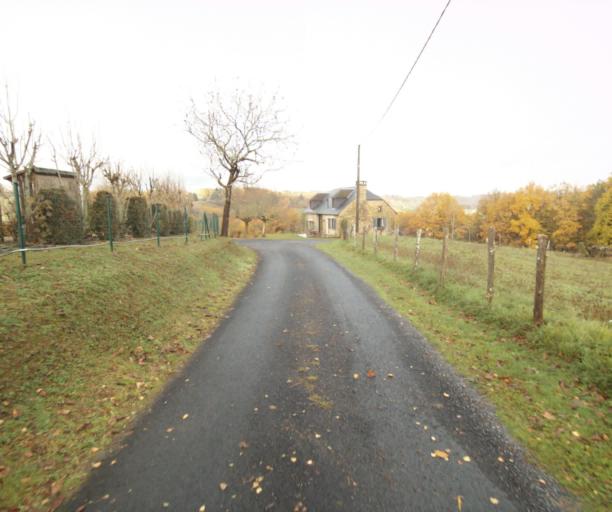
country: FR
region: Limousin
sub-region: Departement de la Correze
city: Cornil
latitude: 45.2276
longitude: 1.6439
